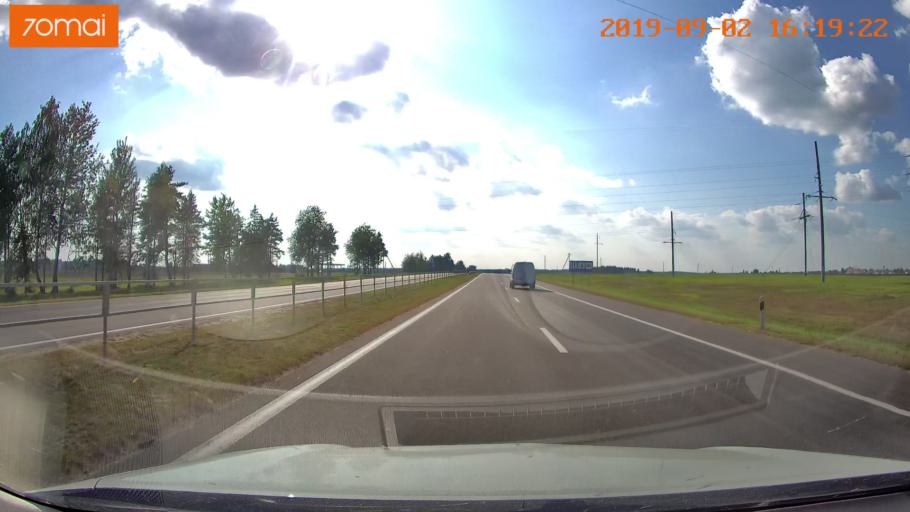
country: BY
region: Minsk
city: Chervyen'
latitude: 53.7254
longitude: 28.4126
